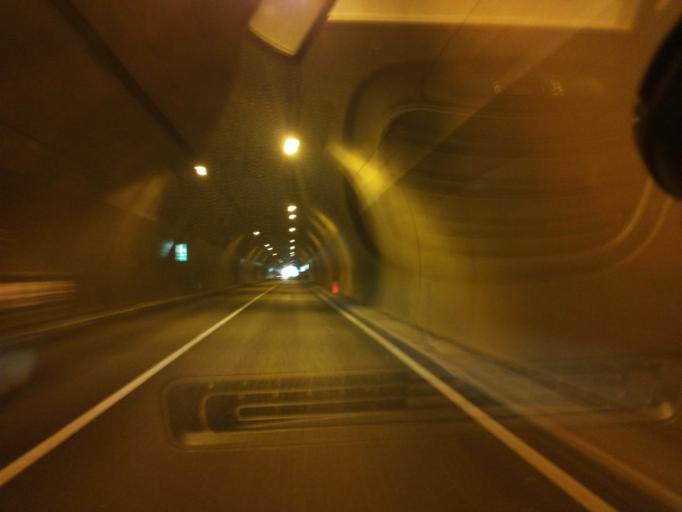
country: IT
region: Piedmont
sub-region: Provincia di Biella
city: Vallanzengo
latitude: 45.6029
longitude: 8.1667
